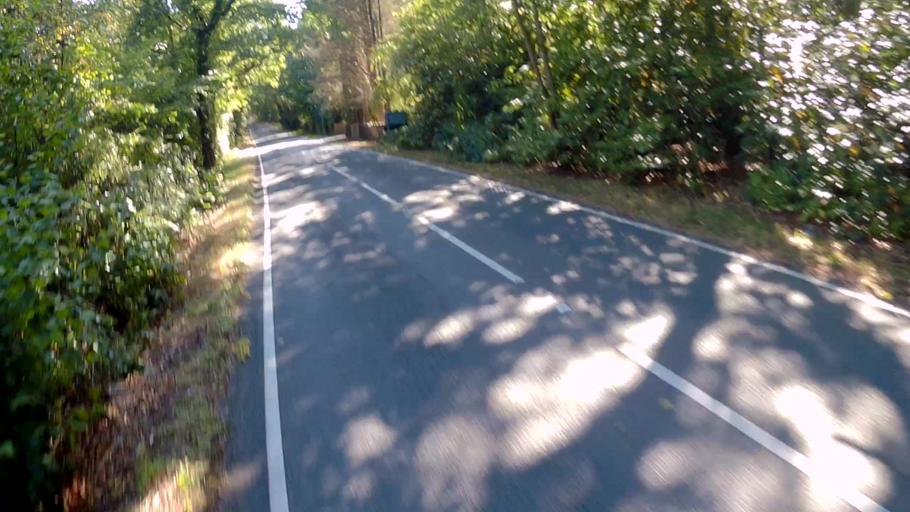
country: GB
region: England
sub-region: Surrey
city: Farnham
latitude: 51.1949
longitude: -0.7719
